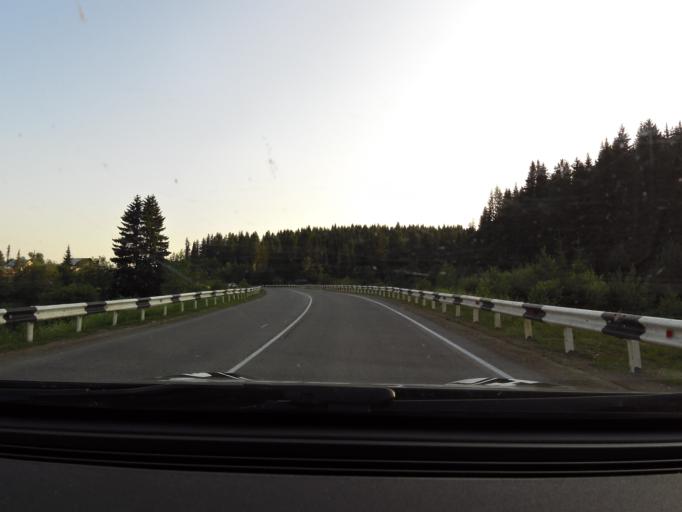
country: RU
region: Sverdlovsk
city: Mikhaylovsk
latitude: 56.4666
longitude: 59.1075
